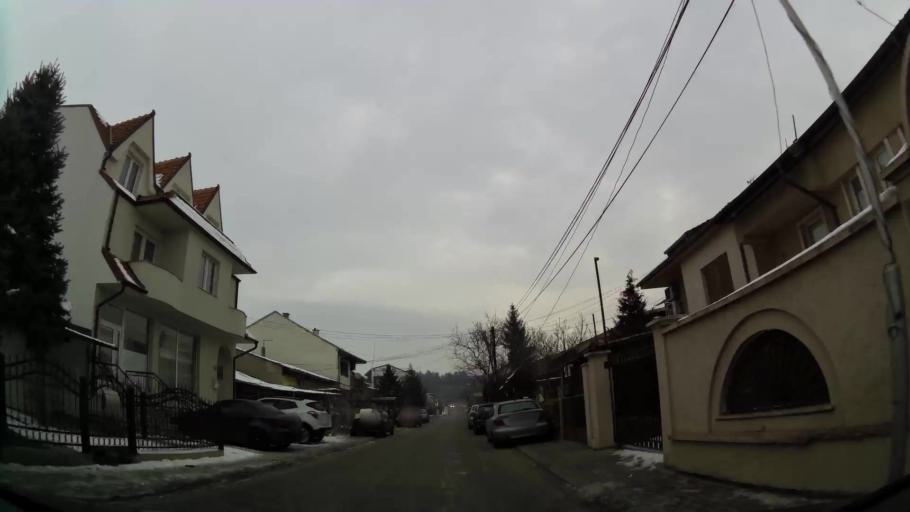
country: MK
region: Saraj
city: Saraj
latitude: 42.0082
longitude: 21.3334
